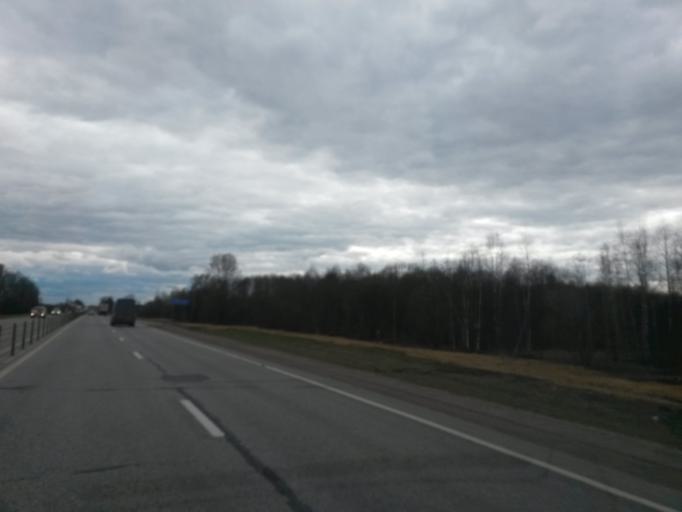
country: RU
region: Jaroslavl
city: Semibratovo
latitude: 57.2814
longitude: 39.5123
